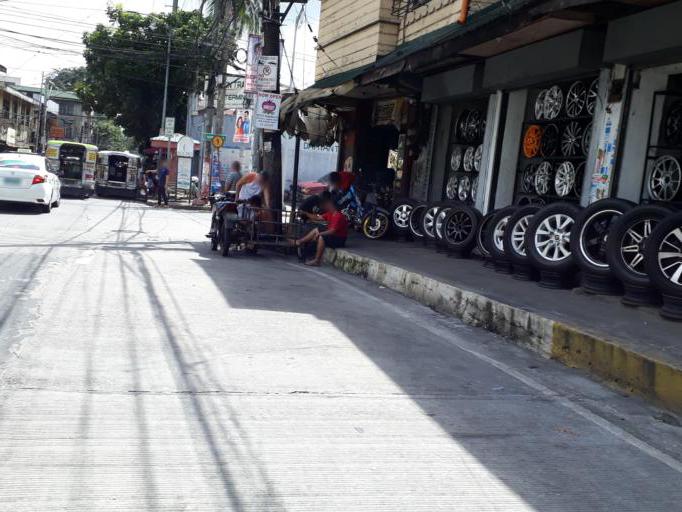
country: PH
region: Metro Manila
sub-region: City of Manila
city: Manila
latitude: 14.6202
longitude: 120.9976
